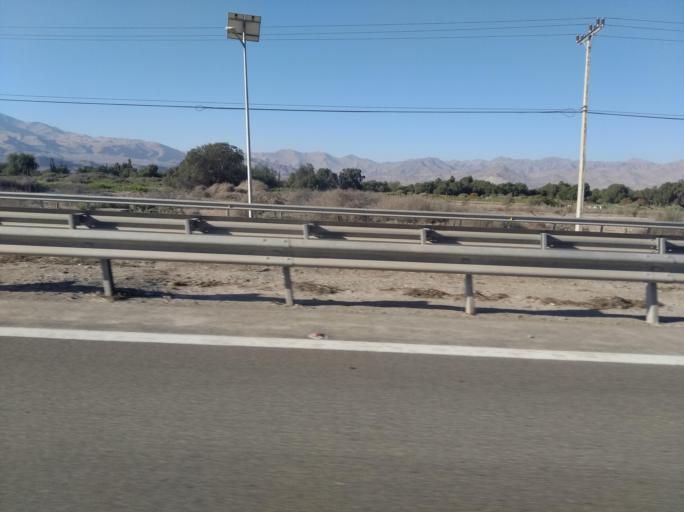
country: CL
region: Atacama
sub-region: Provincia de Copiapo
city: Copiapo
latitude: -27.3082
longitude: -70.4179
